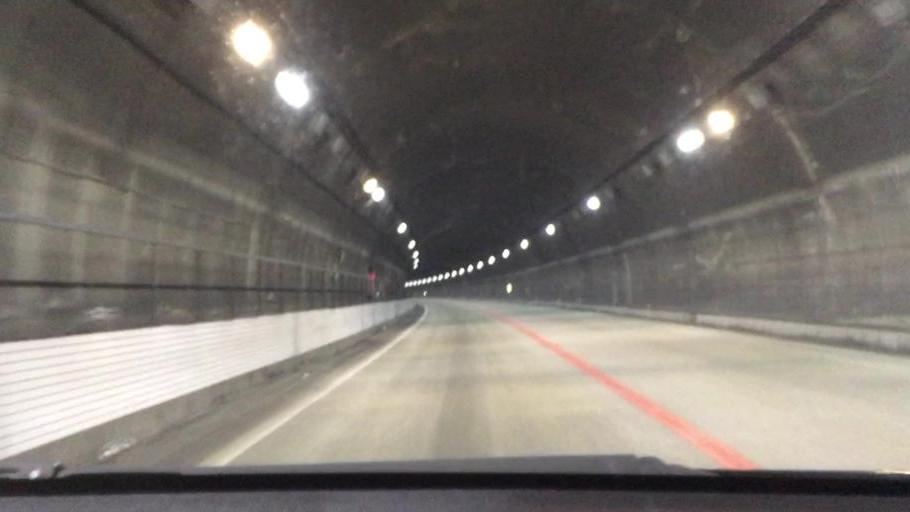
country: JP
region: Yamaguchi
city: Tokuyama
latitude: 34.0687
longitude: 131.8280
